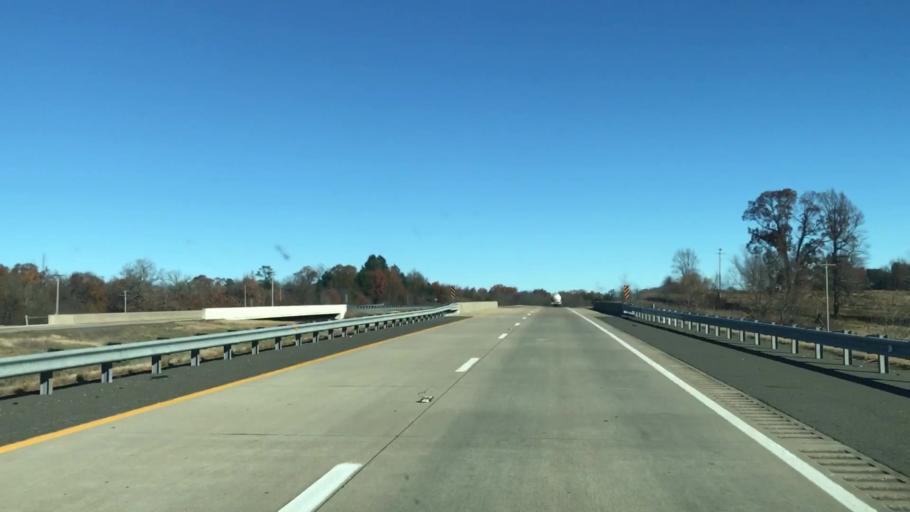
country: US
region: Texas
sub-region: Cass County
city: Queen City
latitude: 33.1527
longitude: -93.8901
